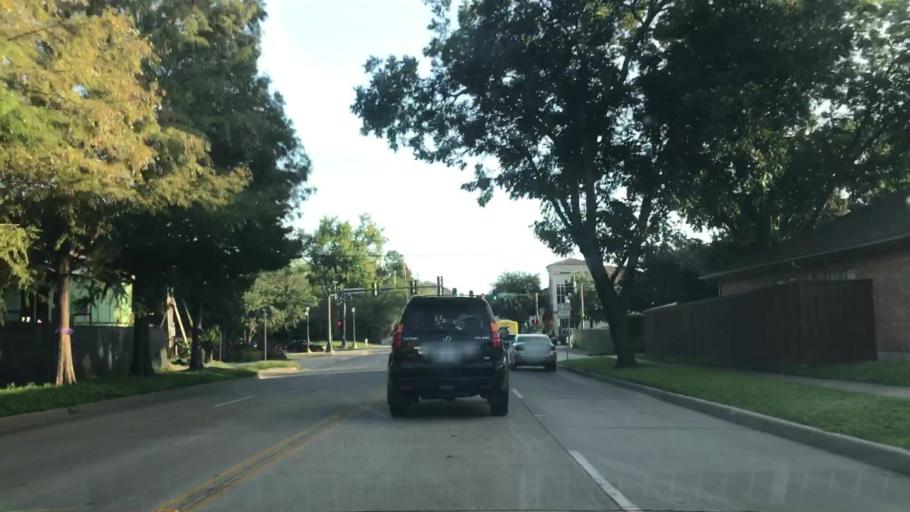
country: US
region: Texas
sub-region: Dallas County
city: University Park
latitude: 32.8520
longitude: -96.7870
